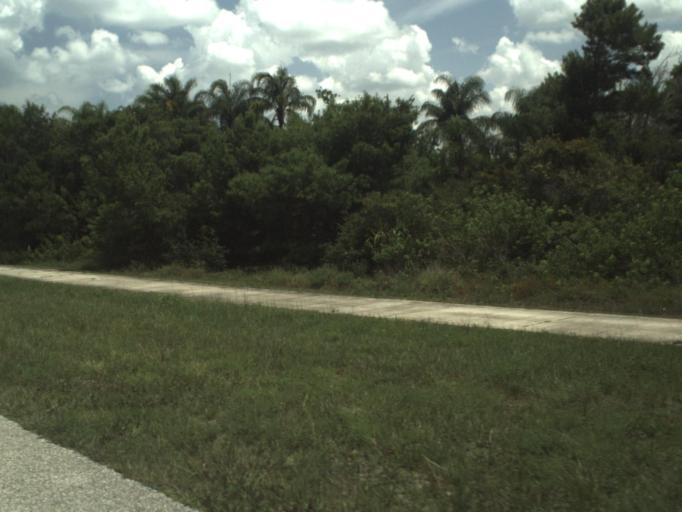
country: US
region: Florida
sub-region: Martin County
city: Hobe Sound
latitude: 27.0476
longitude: -80.1231
